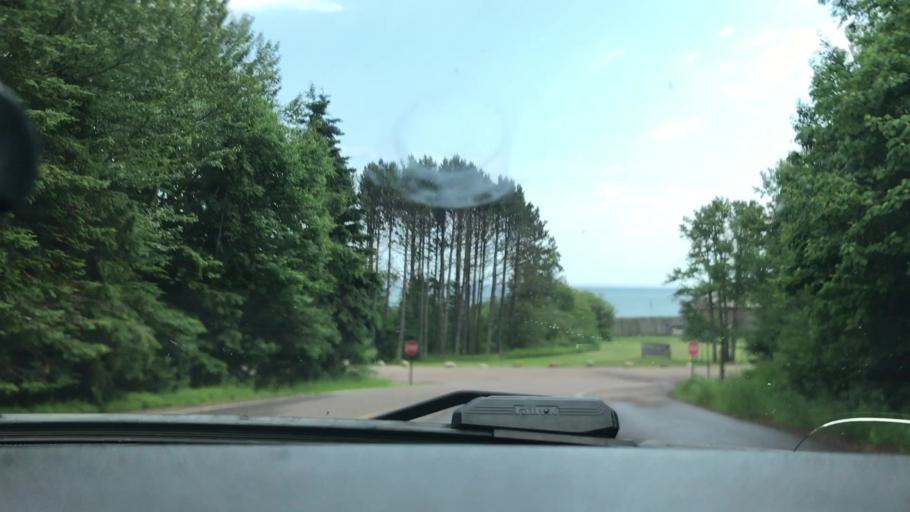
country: CA
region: Ontario
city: Neebing
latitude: 47.9640
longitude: -89.6849
